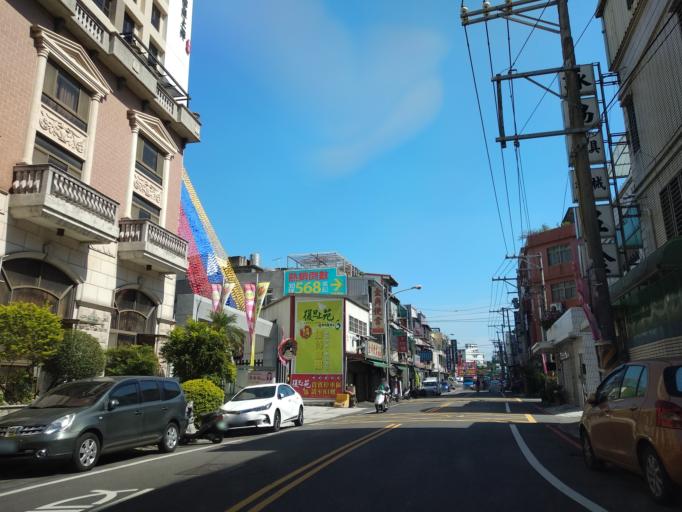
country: TW
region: Taiwan
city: Taoyuan City
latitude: 24.9474
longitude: 121.2089
